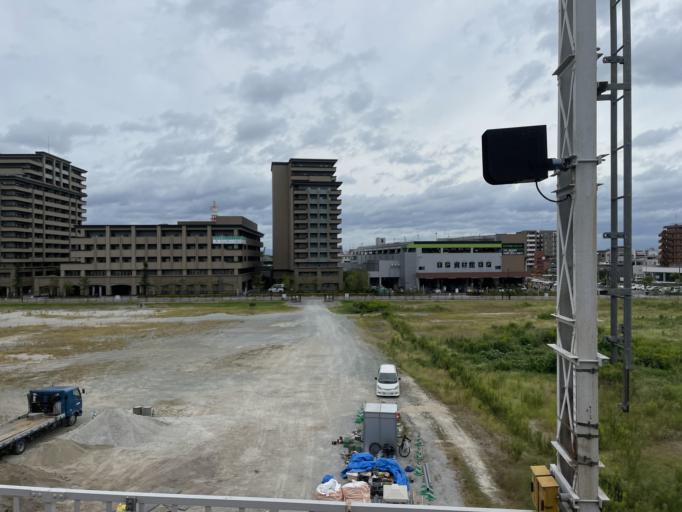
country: JP
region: Hyogo
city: Nishinomiya-hama
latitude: 34.7380
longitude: 135.3552
